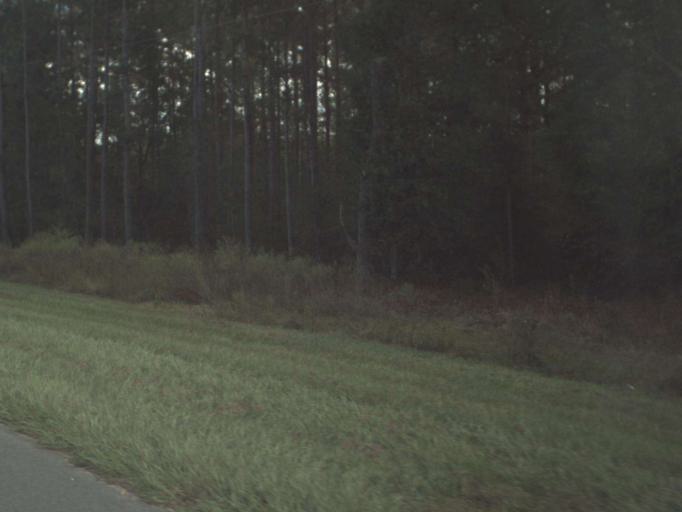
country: US
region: Florida
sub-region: Calhoun County
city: Blountstown
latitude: 30.4434
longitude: -85.0684
